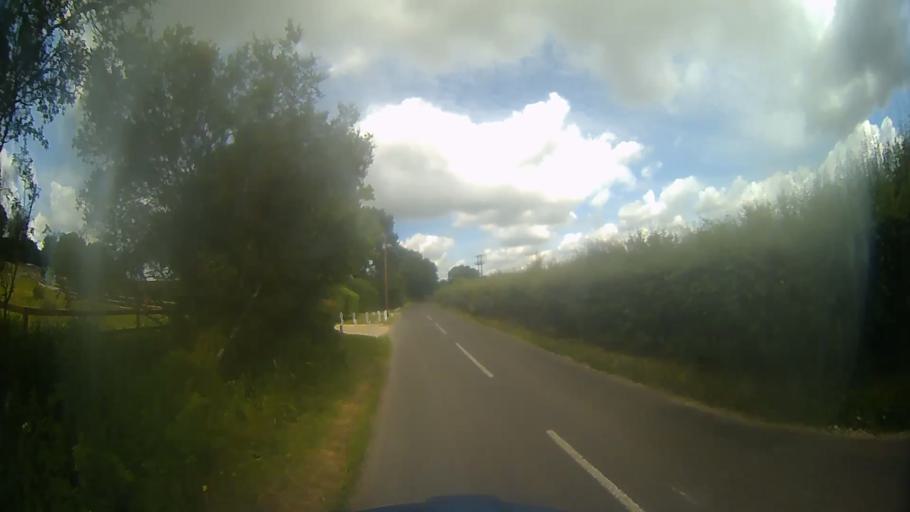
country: GB
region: England
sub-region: Hampshire
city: Andover
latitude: 51.2336
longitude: -1.4603
